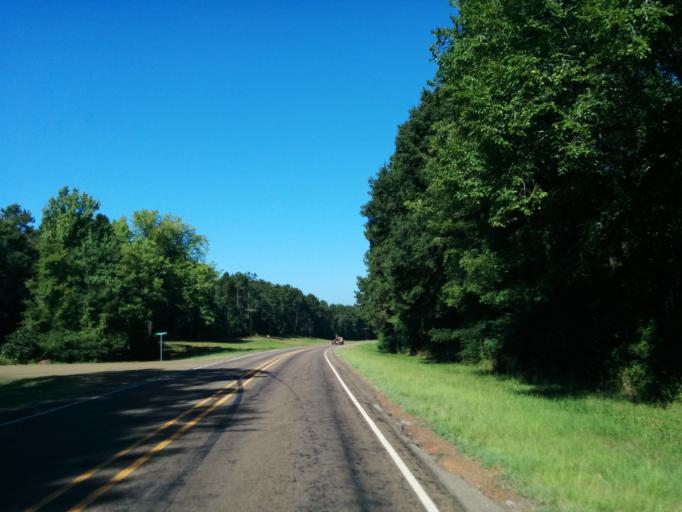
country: US
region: Texas
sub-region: Sabine County
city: Milam
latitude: 31.4304
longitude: -93.7964
